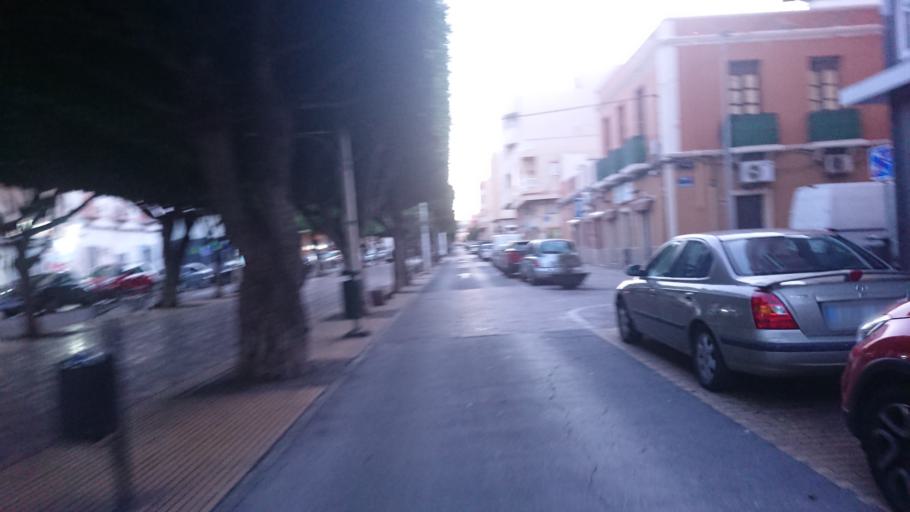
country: ES
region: Melilla
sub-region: Melilla
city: Melilla
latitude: 35.2758
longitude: -2.9431
